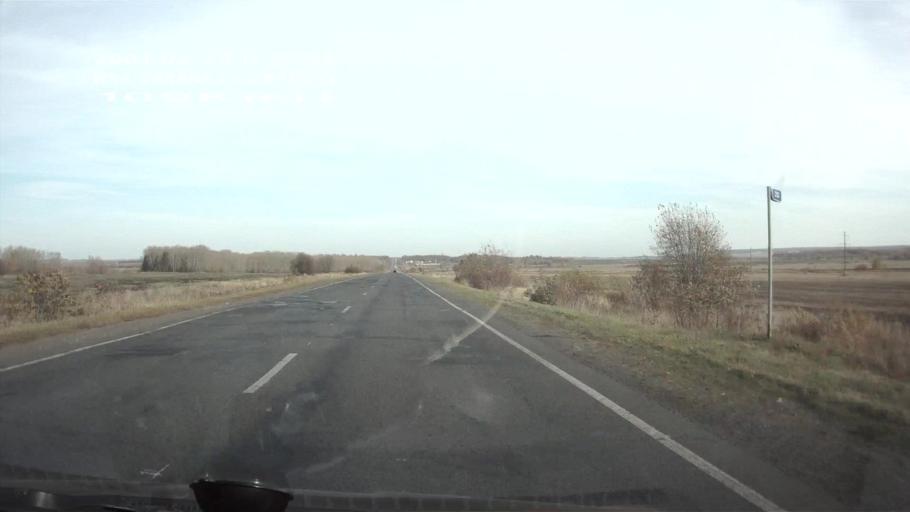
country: RU
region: Mordoviya
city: Atyashevo
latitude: 54.5469
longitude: 45.9483
